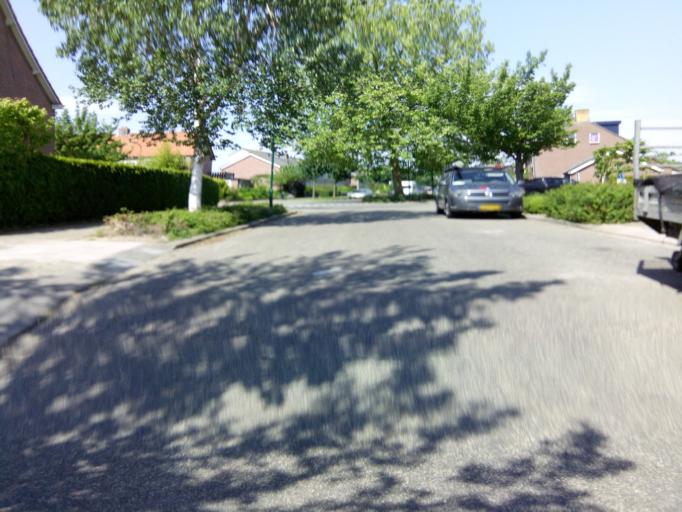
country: NL
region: Utrecht
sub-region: Gemeente Woudenberg
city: Woudenberg
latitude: 52.0829
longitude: 5.4266
